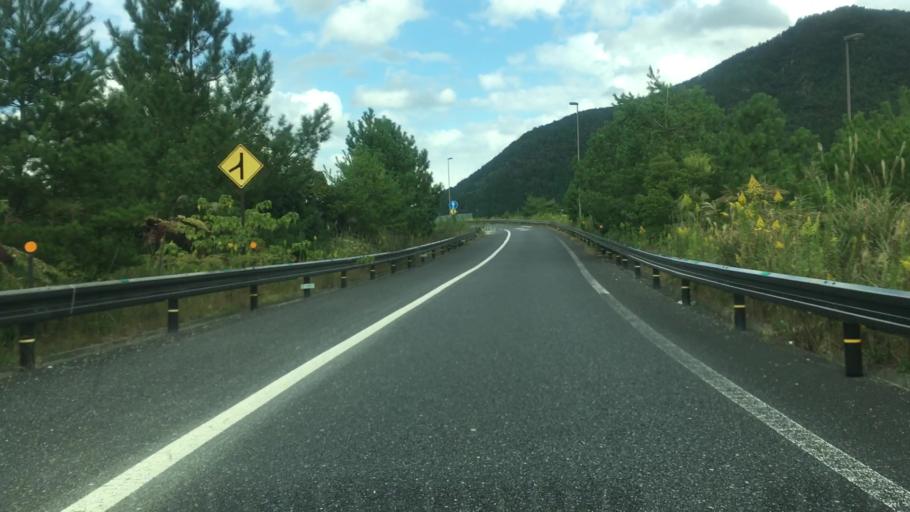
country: JP
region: Kyoto
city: Fukuchiyama
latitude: 35.1627
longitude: 135.0444
